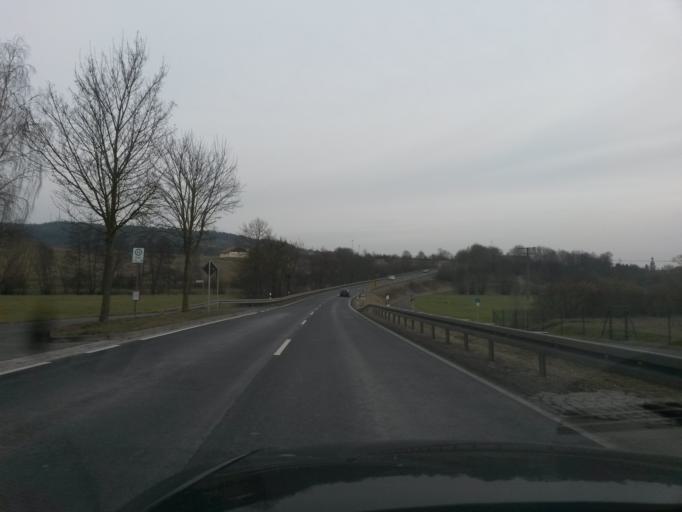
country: DE
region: Bavaria
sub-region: Regierungsbezirk Unterfranken
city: Ostheim vor der Rhon
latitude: 50.4636
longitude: 10.2580
